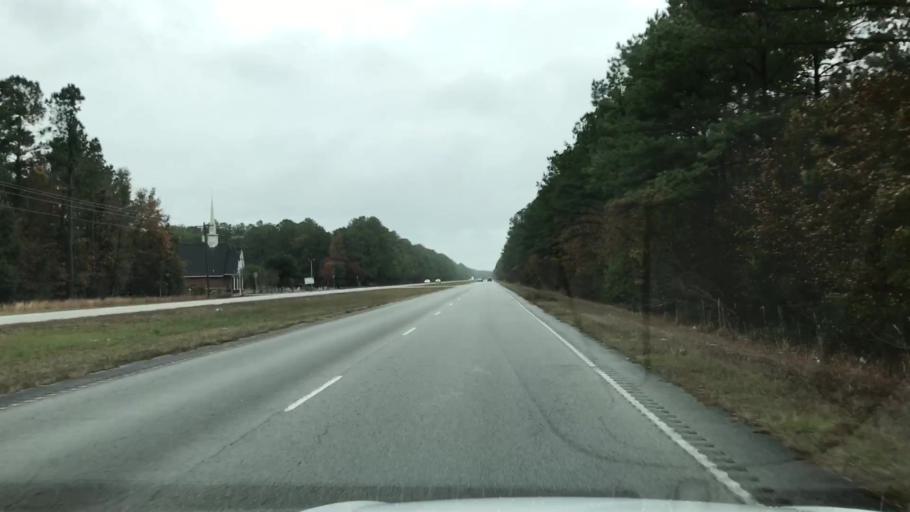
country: US
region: South Carolina
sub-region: Charleston County
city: Awendaw
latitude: 32.9587
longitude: -79.6893
